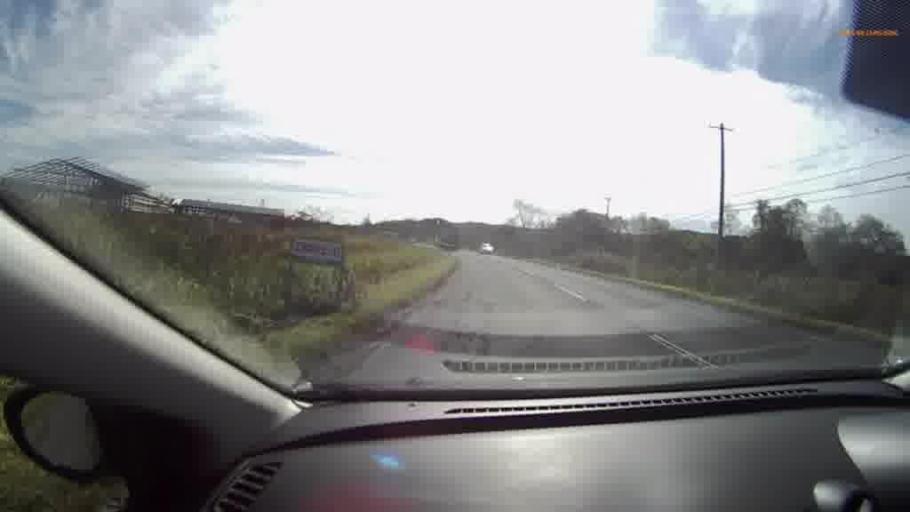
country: JP
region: Hokkaido
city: Kushiro
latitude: 43.0394
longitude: 144.2343
